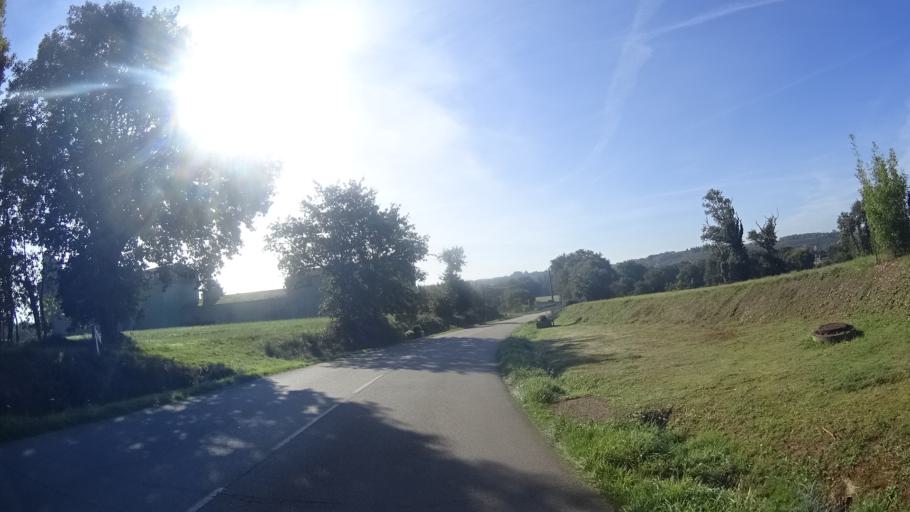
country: FR
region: Brittany
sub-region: Departement du Morbihan
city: Peillac
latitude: 47.7372
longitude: -2.2115
